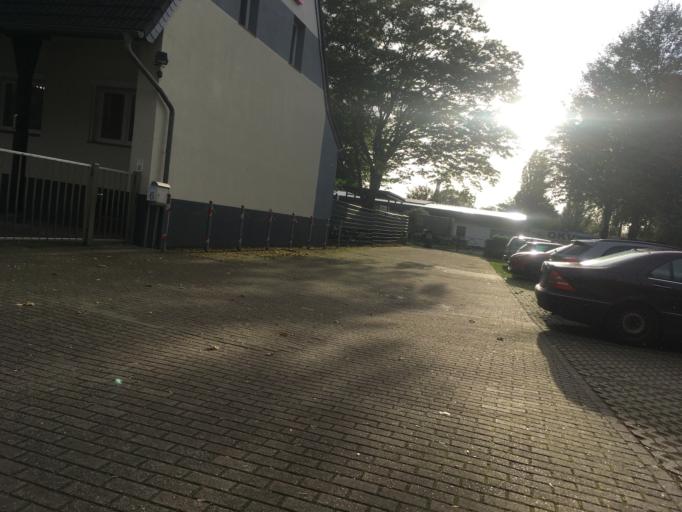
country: DE
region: North Rhine-Westphalia
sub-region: Regierungsbezirk Dusseldorf
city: Oberhausen
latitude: 51.4927
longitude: 6.8536
